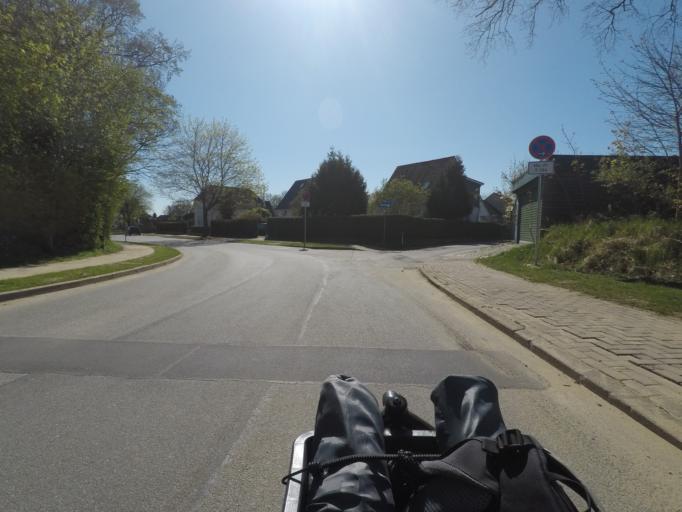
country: DE
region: Schleswig-Holstein
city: Stapelfeld
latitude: 53.6040
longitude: 10.2146
